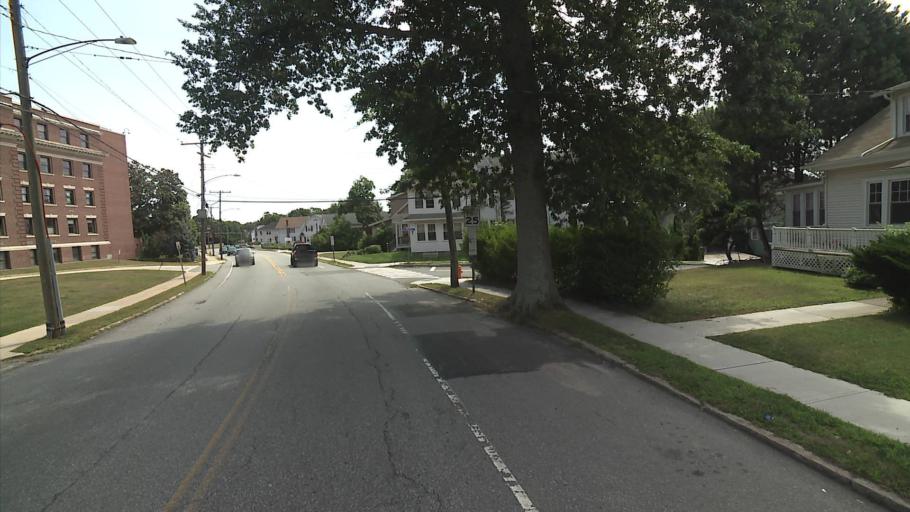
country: US
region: Connecticut
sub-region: New London County
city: New London
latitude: 41.3369
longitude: -72.1070
